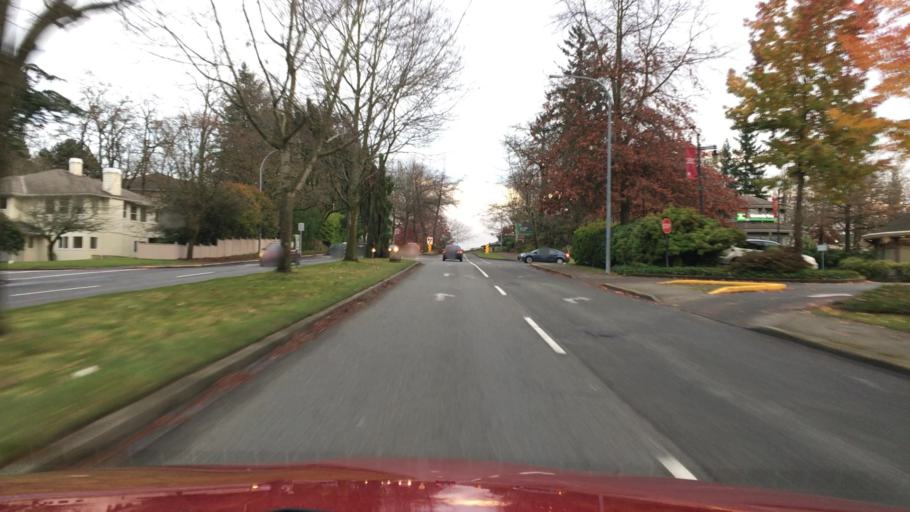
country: CA
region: British Columbia
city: Victoria
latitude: 48.4981
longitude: -123.3804
